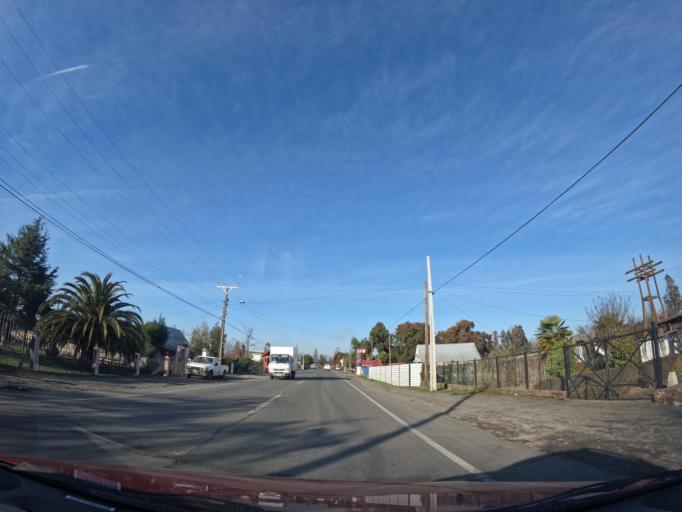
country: CL
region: Maule
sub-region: Provincia de Talca
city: San Clemente
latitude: -35.6225
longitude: -71.4891
